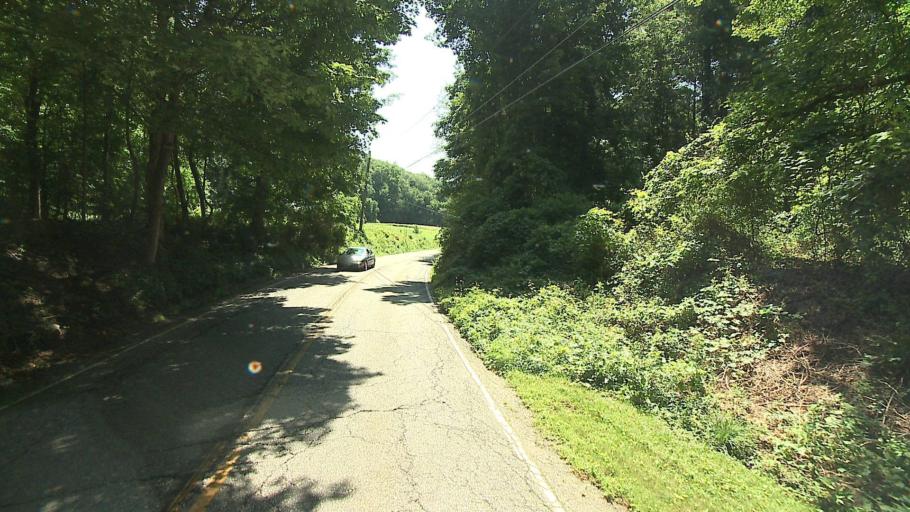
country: US
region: New York
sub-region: Dutchess County
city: Pine Plains
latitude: 41.9217
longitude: -73.4948
